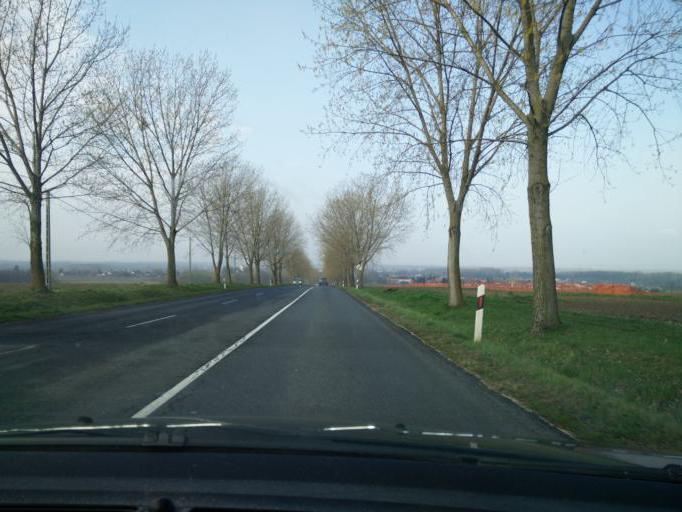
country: HU
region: Somogy
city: Balatonbereny
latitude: 46.6921
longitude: 17.3161
